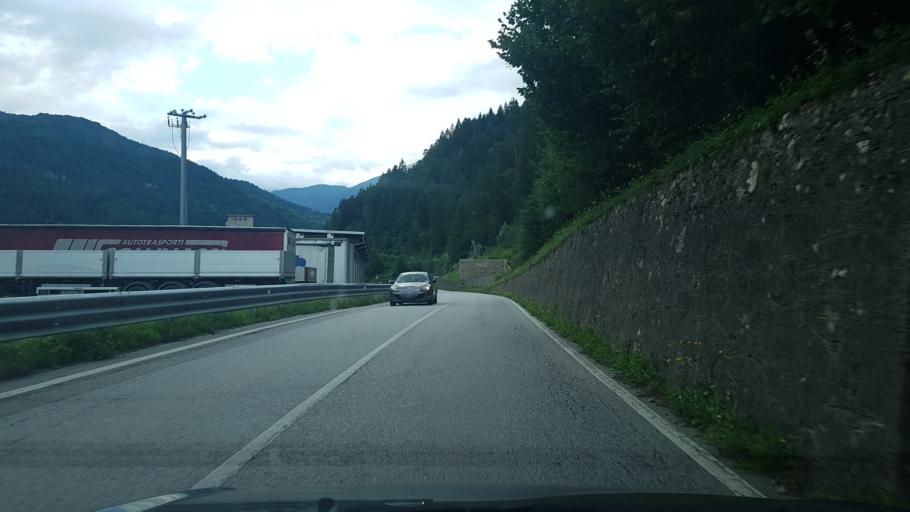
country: IT
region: Friuli Venezia Giulia
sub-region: Provincia di Udine
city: Comeglians
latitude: 46.5014
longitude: 12.8654
